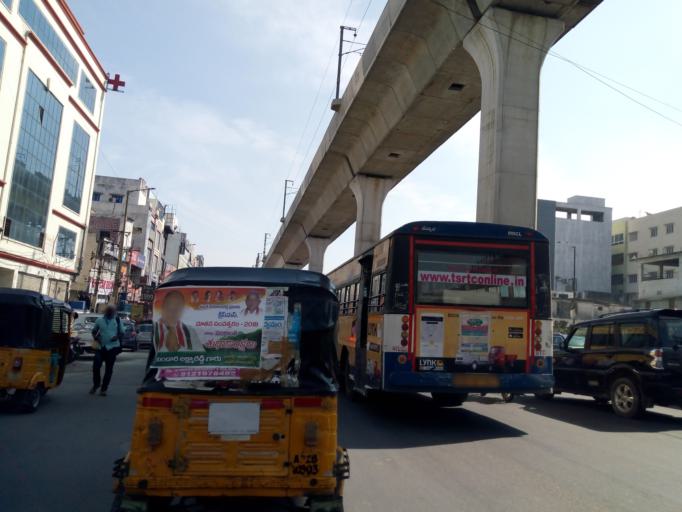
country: IN
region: Telangana
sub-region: Rangareddi
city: Uppal Kalan
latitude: 17.4188
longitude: 78.5419
